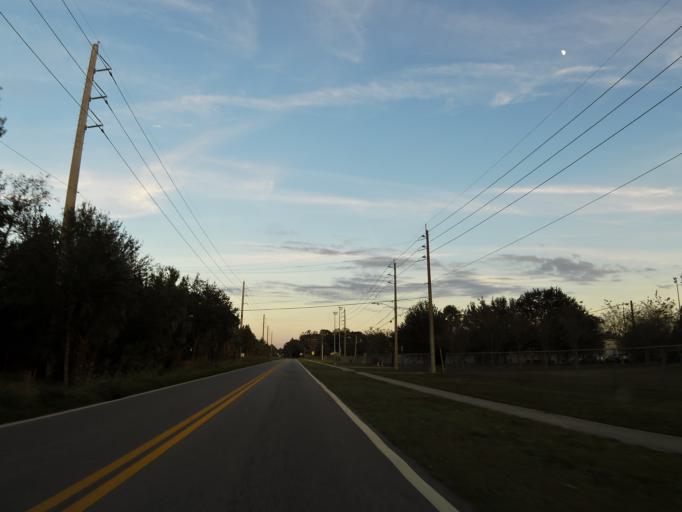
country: US
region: Florida
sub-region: Duval County
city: Jacksonville
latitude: 30.3510
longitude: -81.7262
